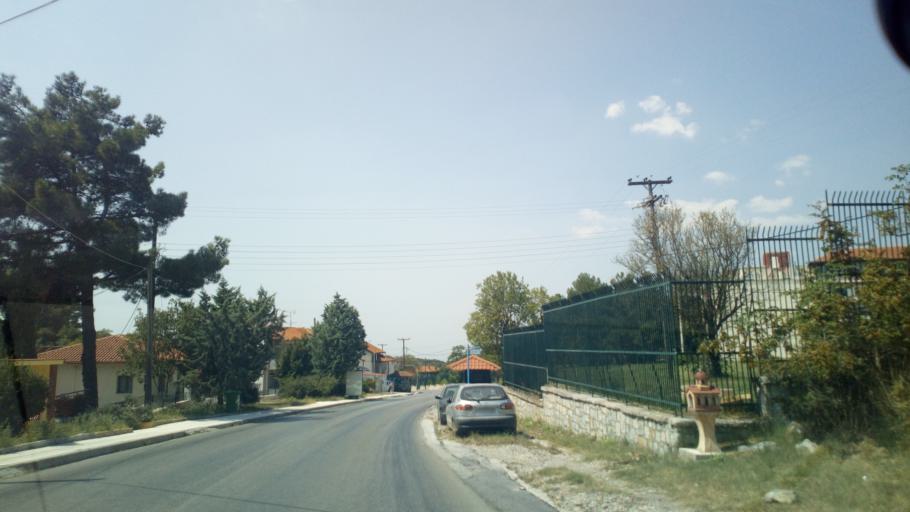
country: GR
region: Central Macedonia
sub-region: Nomos Thessalonikis
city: Asvestochori
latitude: 40.6288
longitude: 23.0479
